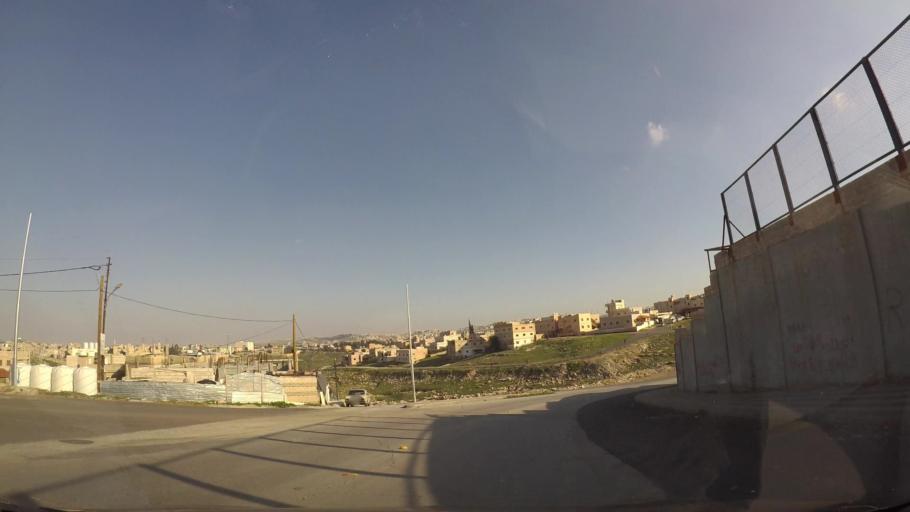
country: JO
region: Amman
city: Amman
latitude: 31.9767
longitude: 35.9647
